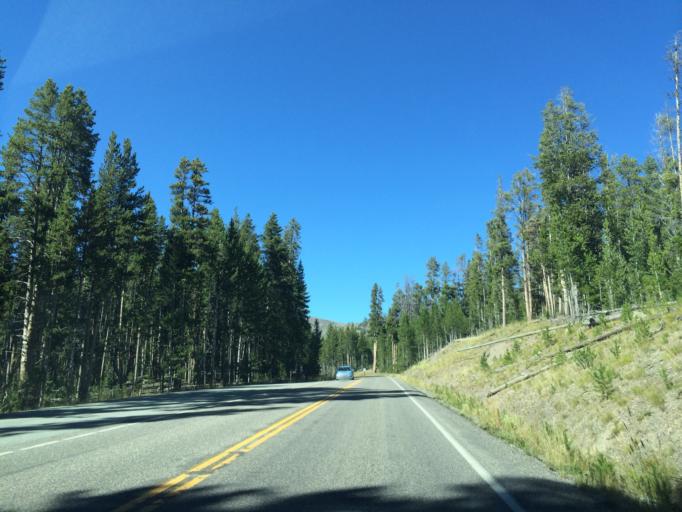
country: US
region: Montana
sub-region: Gallatin County
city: West Yellowstone
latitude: 44.7386
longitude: -110.4931
